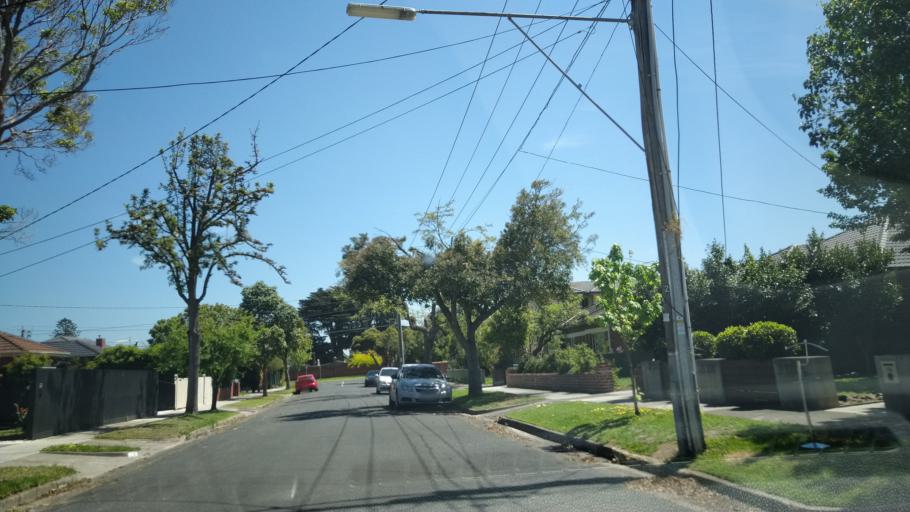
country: AU
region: Victoria
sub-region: Glen Eira
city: Caulfield South
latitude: -37.8994
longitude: 145.0244
